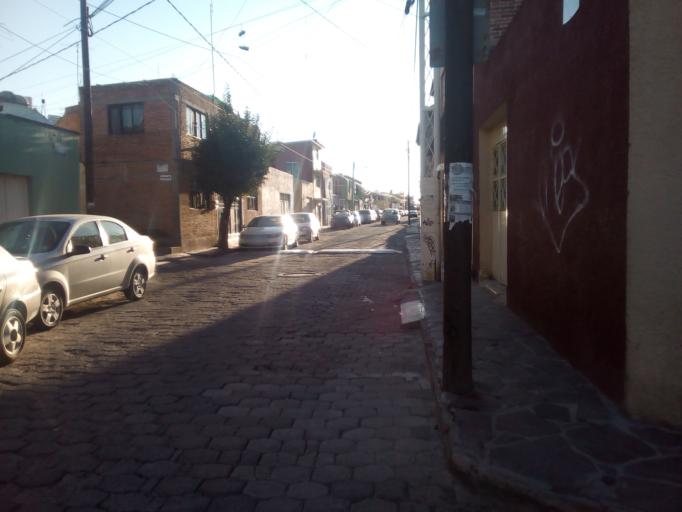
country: MX
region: Guerrero
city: San Luis de la Paz
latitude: 21.2943
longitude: -100.5162
